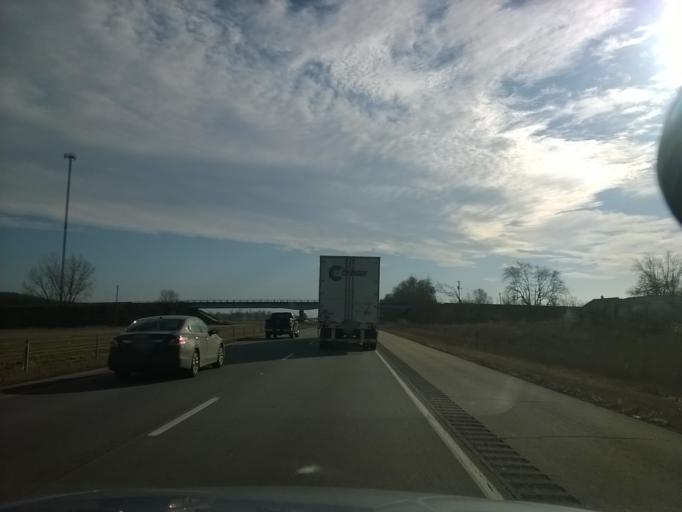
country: US
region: Indiana
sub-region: Johnson County
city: Edinburgh
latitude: 39.3784
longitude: -85.9429
